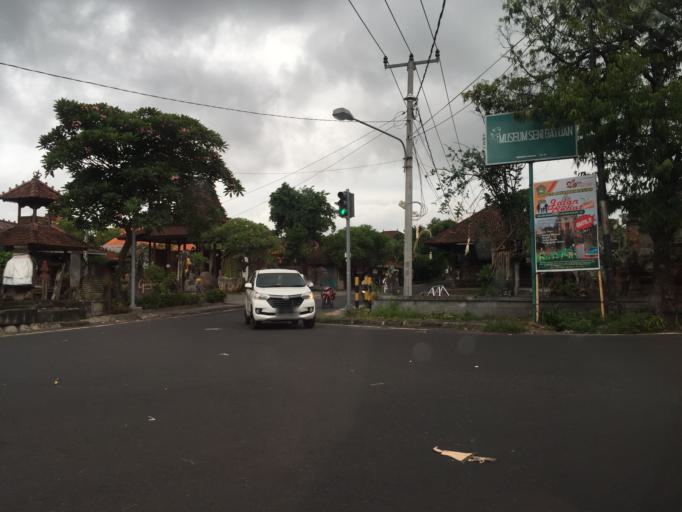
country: ID
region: Bali
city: Banjar Desa
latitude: -8.5816
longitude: 115.2781
